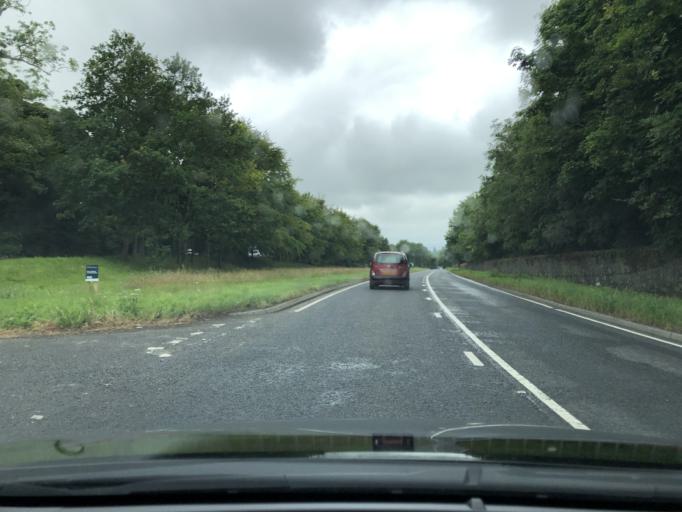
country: GB
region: Northern Ireland
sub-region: Down District
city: Dundrum
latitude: 54.3205
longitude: -5.8374
